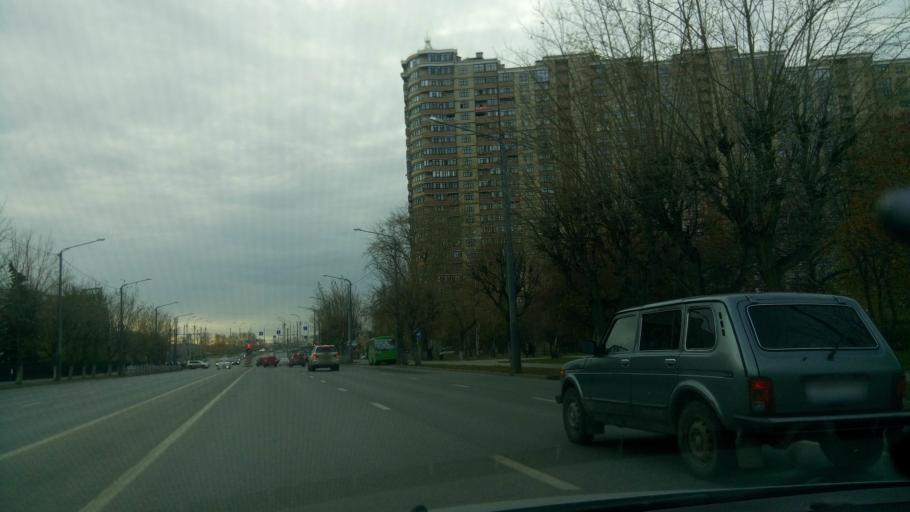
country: RU
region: Tjumen
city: Tyumen
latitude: 57.1361
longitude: 65.5662
